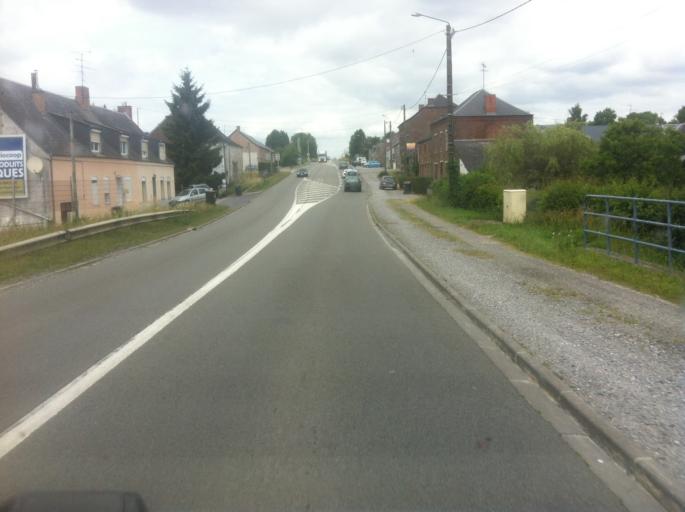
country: FR
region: Nord-Pas-de-Calais
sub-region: Departement du Nord
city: Avesnelles
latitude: 50.1742
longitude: 3.9530
